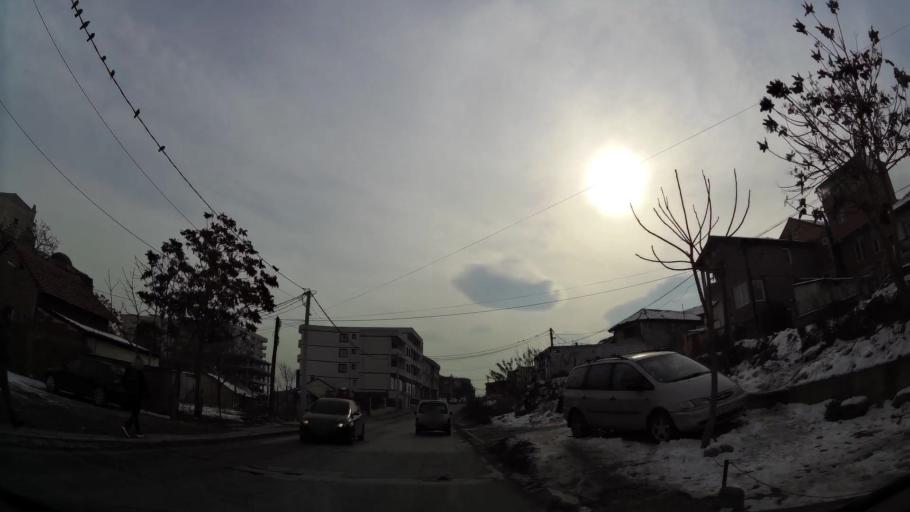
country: MK
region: Cair
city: Cair
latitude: 42.0112
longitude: 21.4328
